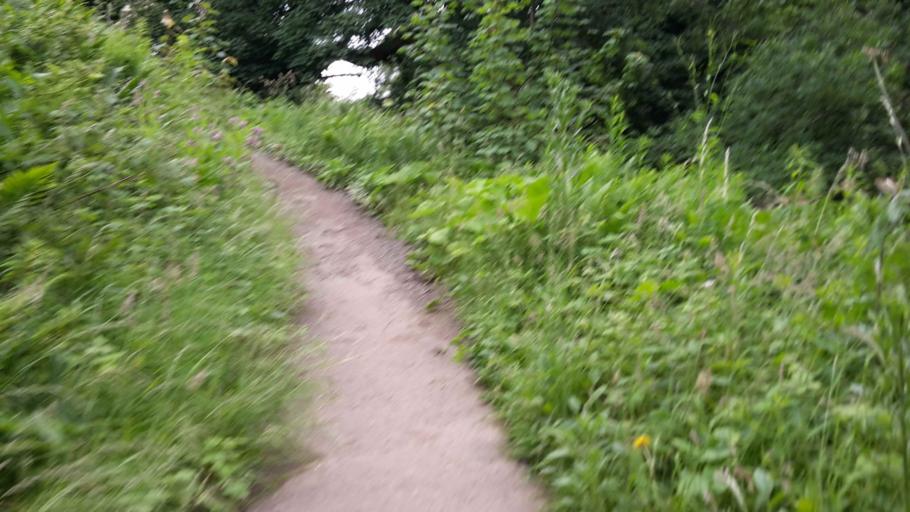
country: GB
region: Scotland
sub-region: South Lanarkshire
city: Uddingston
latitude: 55.8094
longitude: -4.0963
